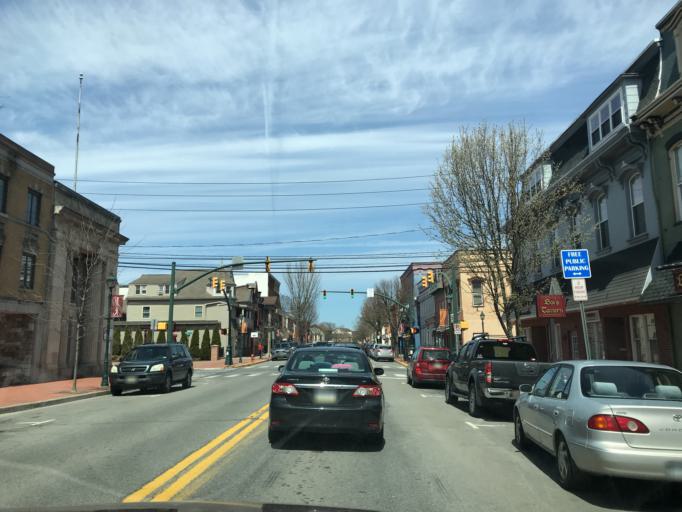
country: US
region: Pennsylvania
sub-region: Snyder County
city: Selinsgrove
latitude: 40.7990
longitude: -76.8621
